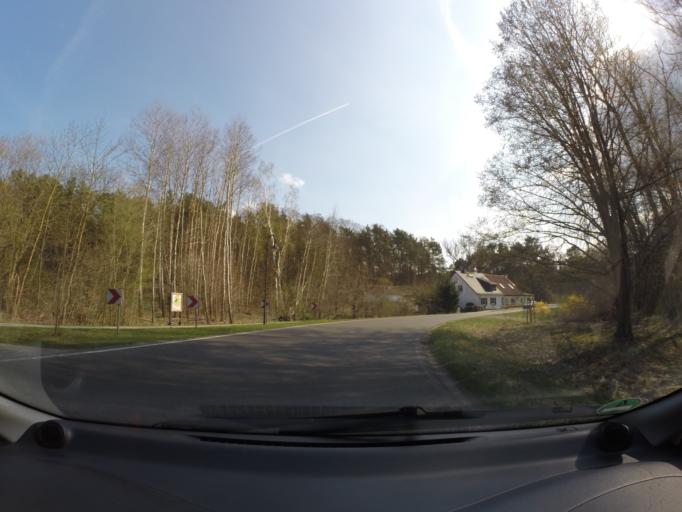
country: DE
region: Brandenburg
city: Rehfelde
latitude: 52.4609
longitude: 13.9582
